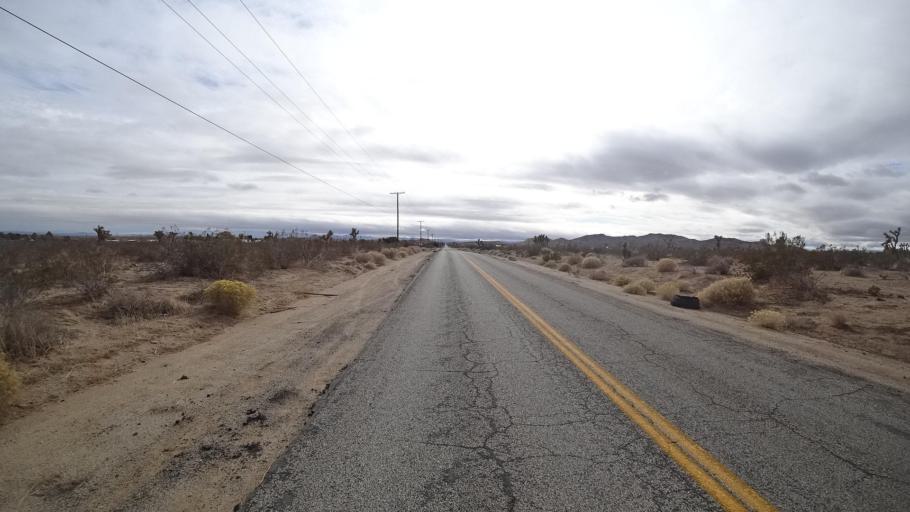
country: US
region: California
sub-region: Kern County
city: Rosamond
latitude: 34.9542
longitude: -118.2126
